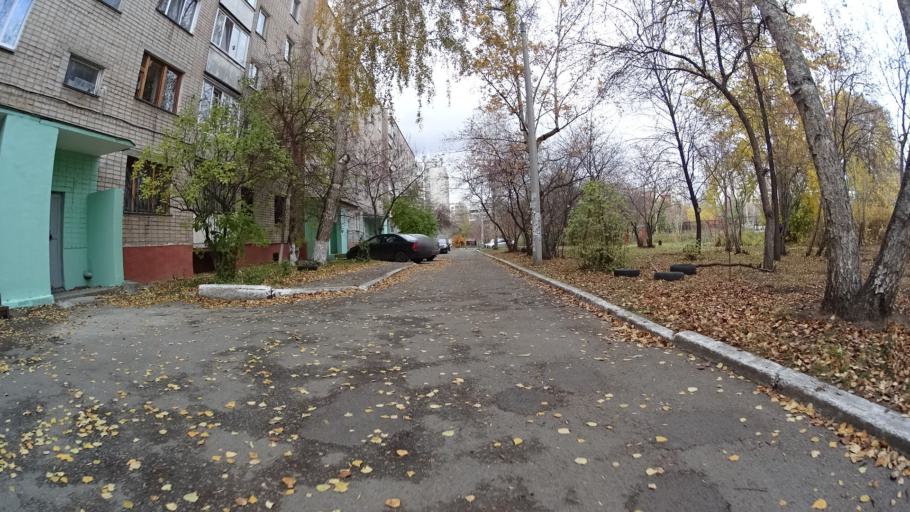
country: RU
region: Chelyabinsk
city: Roshchino
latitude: 55.1916
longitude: 61.3069
